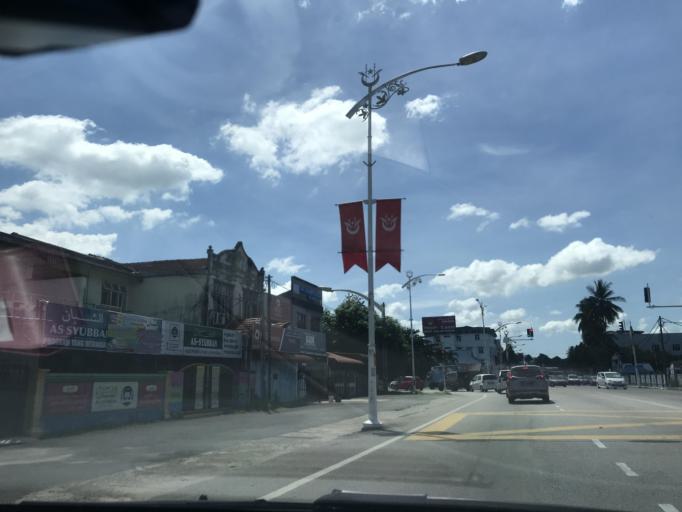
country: MY
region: Kelantan
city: Kota Bharu
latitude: 6.1083
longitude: 102.2541
